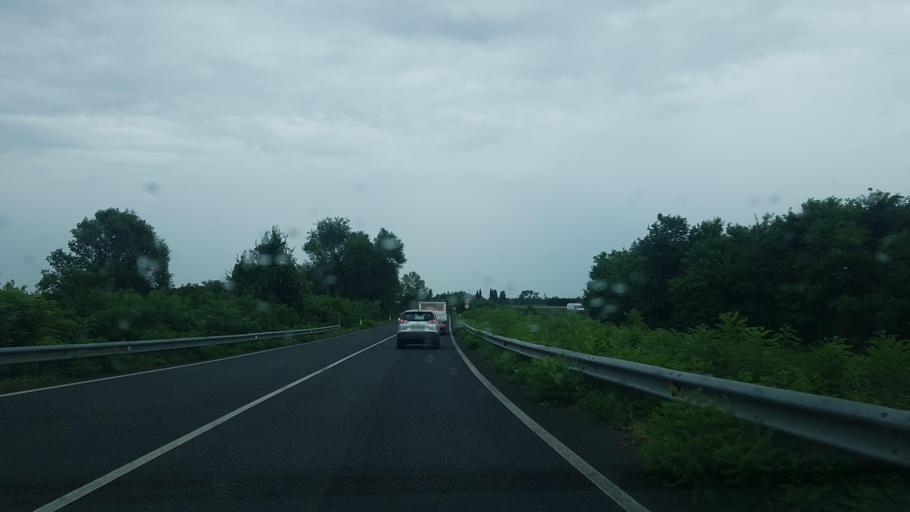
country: IT
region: Friuli Venezia Giulia
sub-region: Provincia di Udine
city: Sevegliano
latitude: 45.8914
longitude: 13.3177
